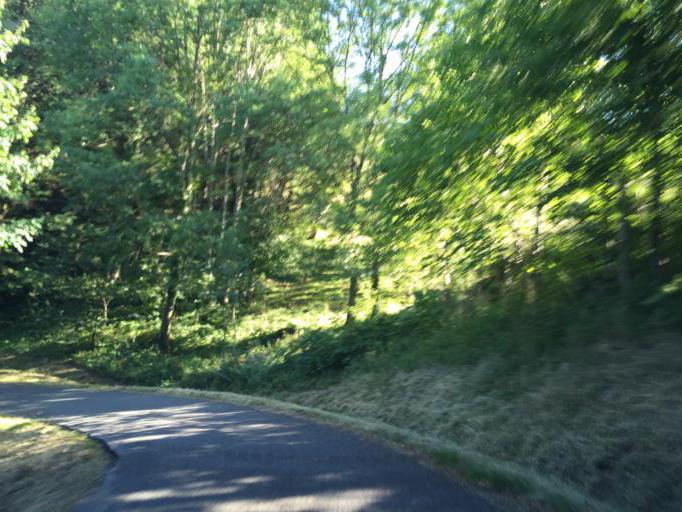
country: FR
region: Rhone-Alpes
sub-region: Departement de la Loire
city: Saint-Jean-Bonnefonds
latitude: 45.4309
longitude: 4.4787
